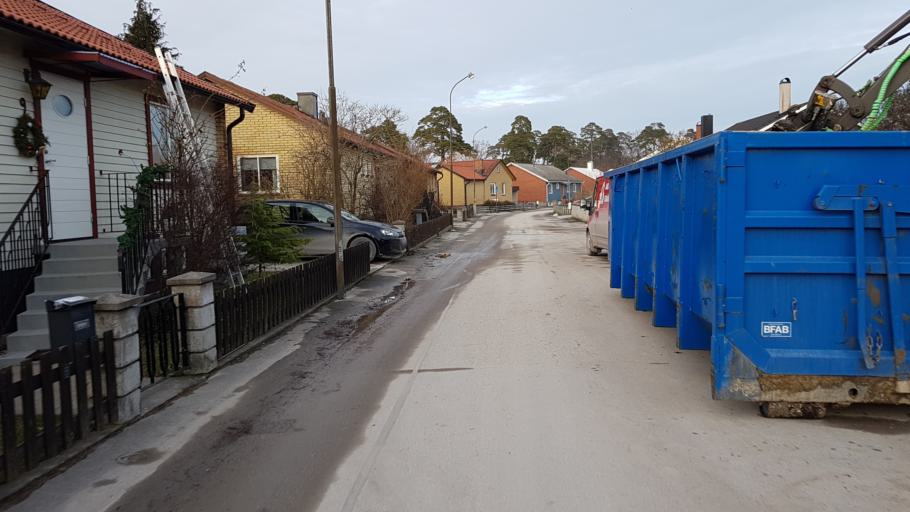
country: SE
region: Gotland
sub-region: Gotland
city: Visby
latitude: 57.6221
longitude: 18.2933
